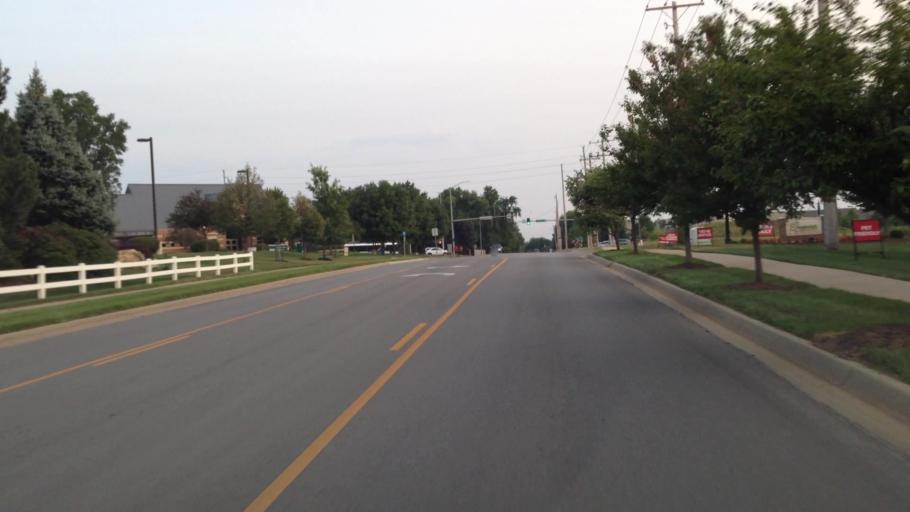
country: US
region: Kansas
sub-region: Douglas County
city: Lawrence
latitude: 38.9731
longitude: -95.2976
